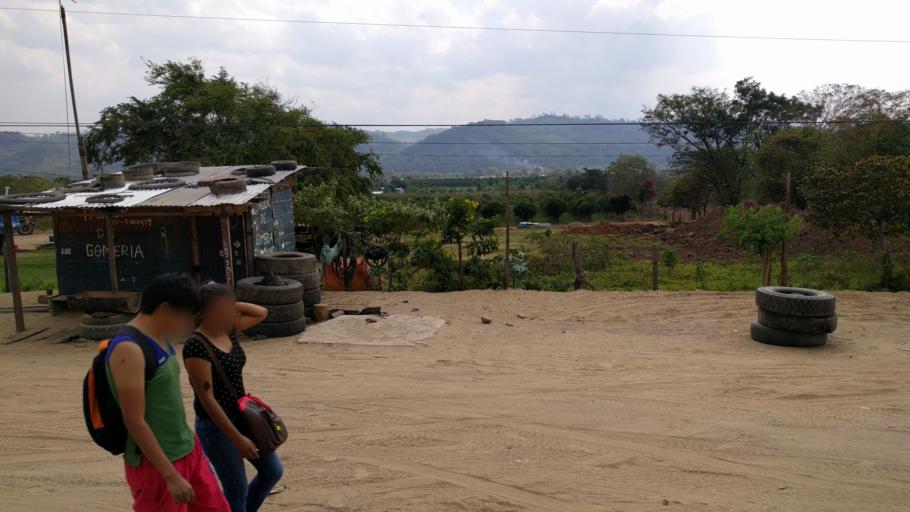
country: BO
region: Santa Cruz
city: Limoncito
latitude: -18.0198
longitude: -63.3977
